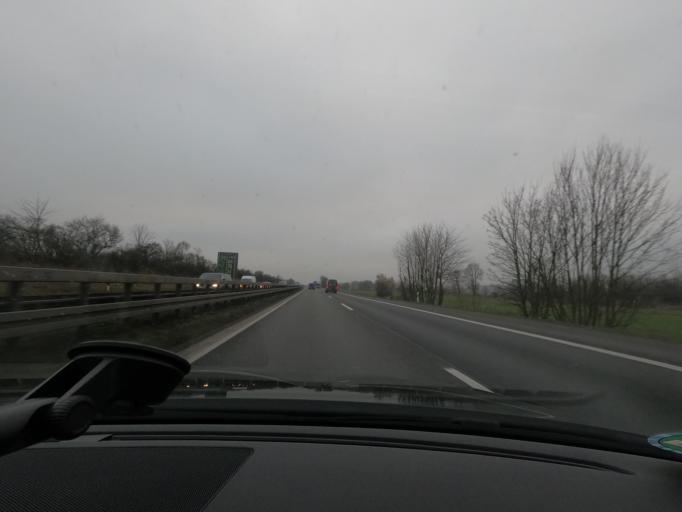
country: DE
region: North Rhine-Westphalia
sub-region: Regierungsbezirk Dusseldorf
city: Monchengladbach
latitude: 51.1471
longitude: 6.4126
